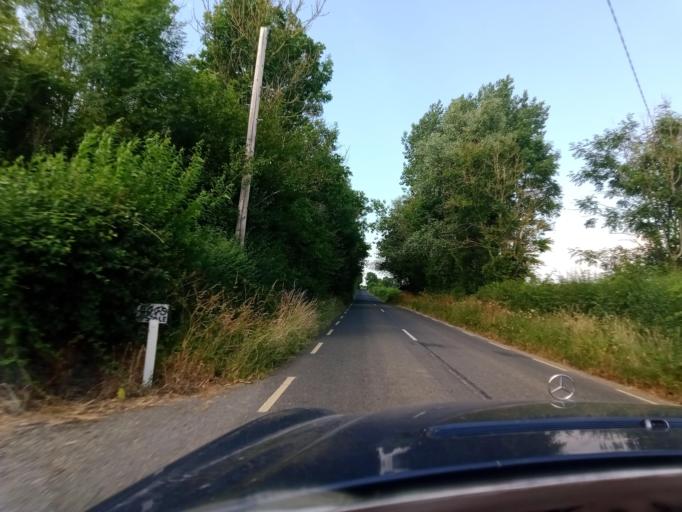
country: IE
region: Leinster
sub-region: Kilkenny
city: Callan
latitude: 52.4957
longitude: -7.3176
